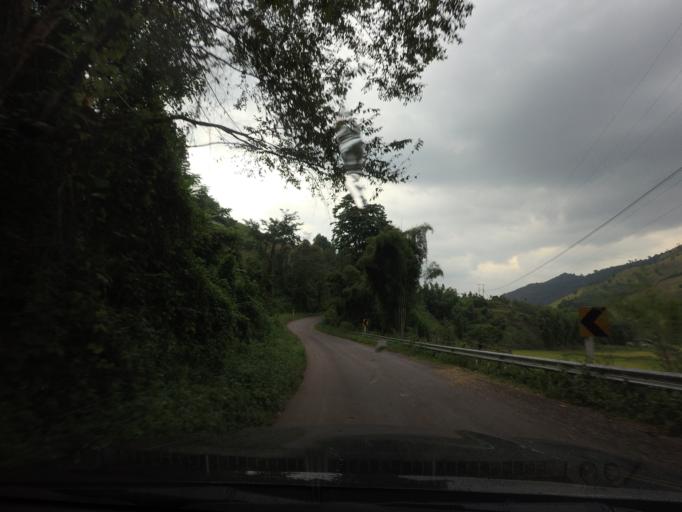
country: TH
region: Nan
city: Bo Kluea
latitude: 19.3325
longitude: 101.1667
